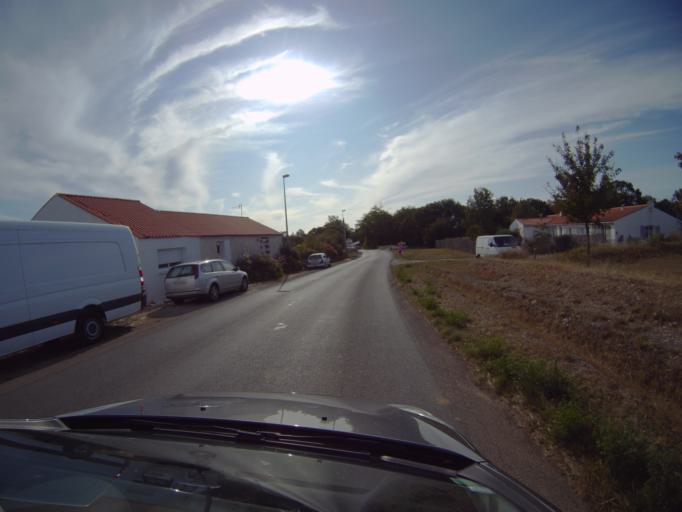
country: FR
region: Pays de la Loire
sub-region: Departement de la Vendee
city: Angles
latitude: 46.4067
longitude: -1.4180
